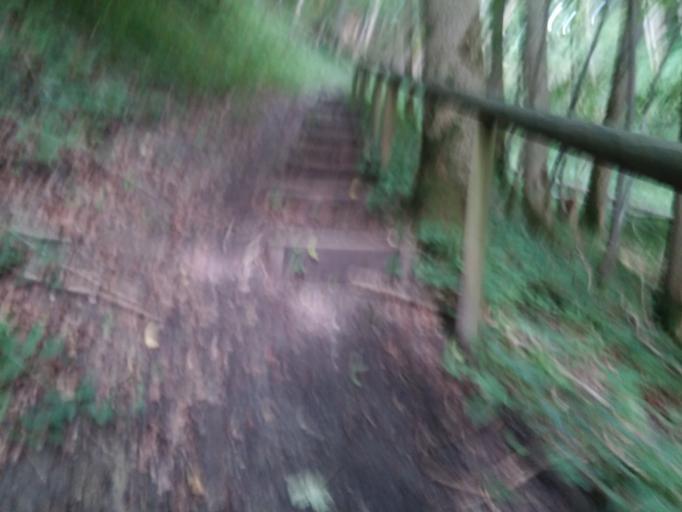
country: DE
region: Bavaria
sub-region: Swabia
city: Kronburg
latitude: 47.8629
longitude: 10.1872
